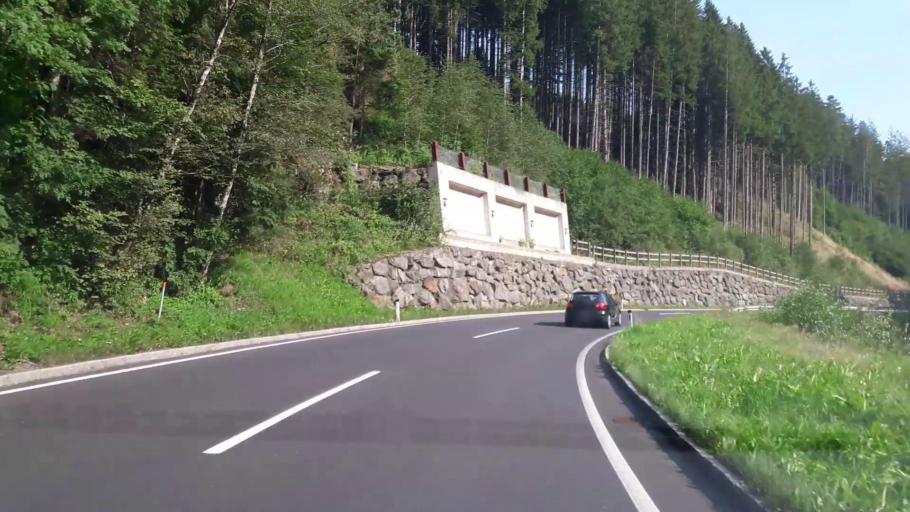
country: AT
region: Styria
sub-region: Politischer Bezirk Weiz
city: Birkfeld
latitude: 47.3367
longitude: 15.6877
